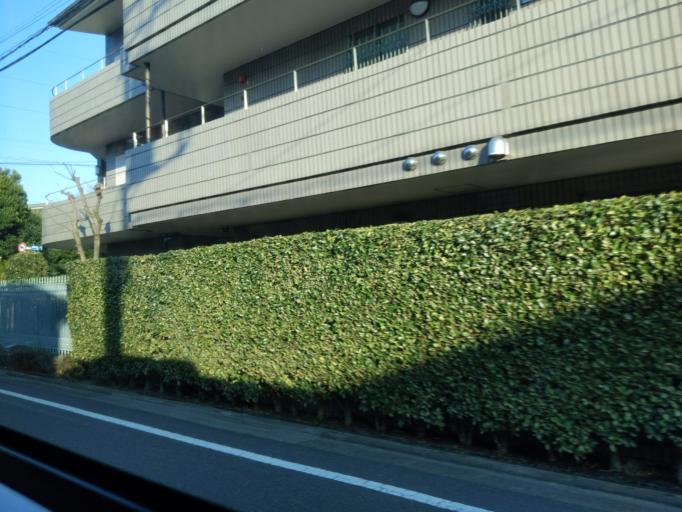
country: JP
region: Tokyo
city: Tokyo
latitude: 35.6337
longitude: 139.6959
